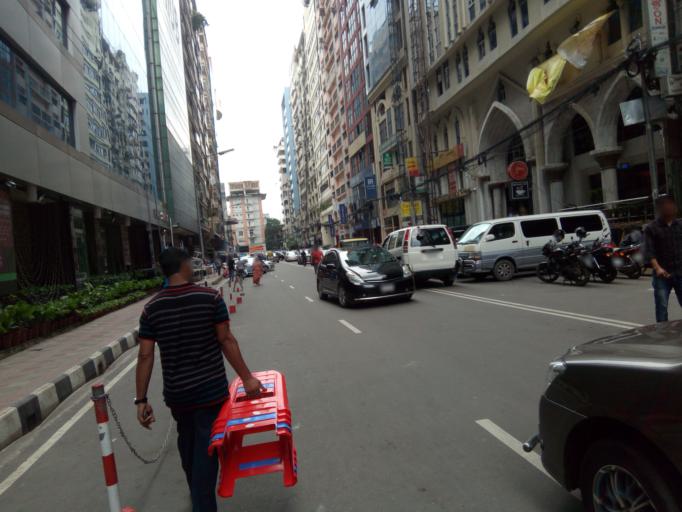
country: BD
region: Dhaka
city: Paltan
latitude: 23.7935
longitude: 90.4048
